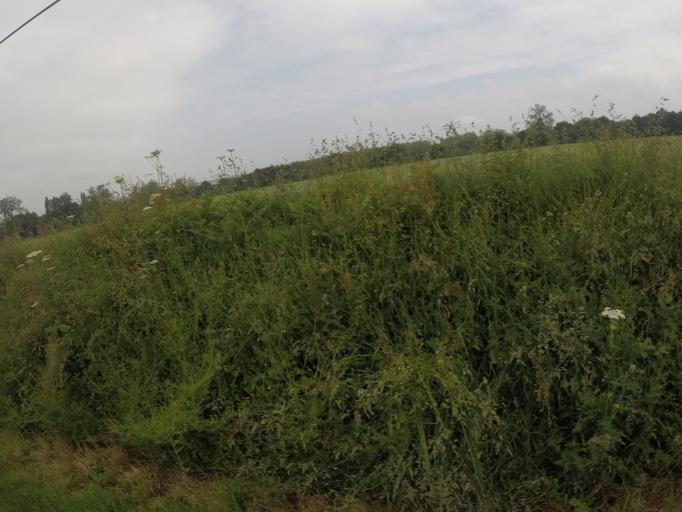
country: FR
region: Brittany
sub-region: Departement des Cotes-d'Armor
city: Goudelin
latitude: 48.6271
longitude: -3.0453
